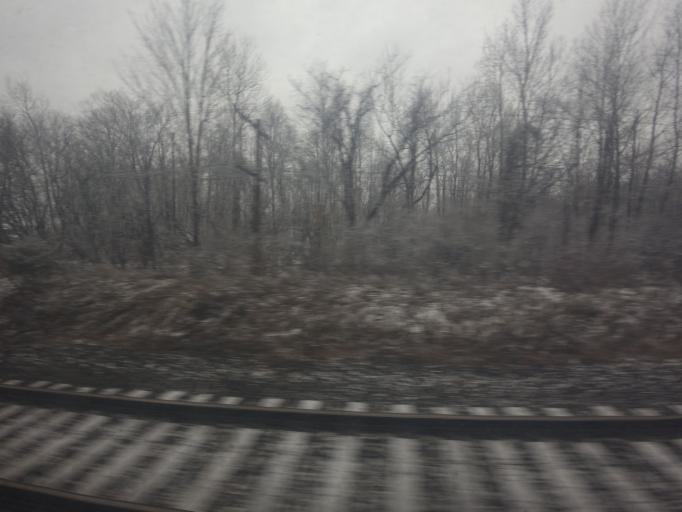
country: US
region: New York
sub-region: Jefferson County
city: Alexandria Bay
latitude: 44.4904
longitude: -75.8736
